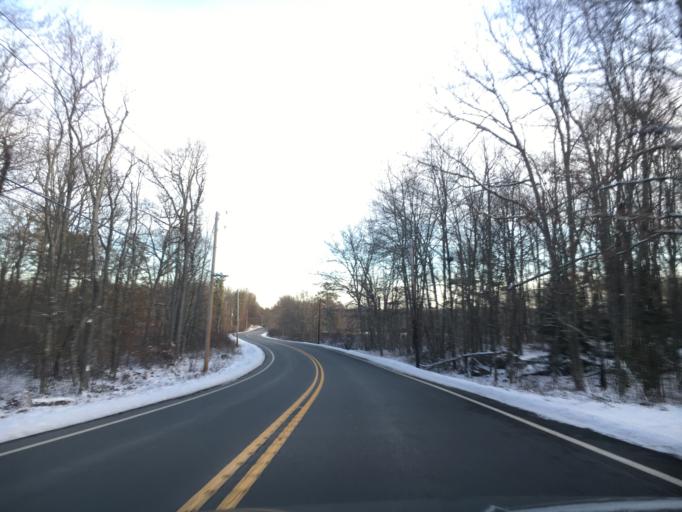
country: US
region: Pennsylvania
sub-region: Pike County
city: Hemlock Farms
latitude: 41.2576
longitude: -75.0781
